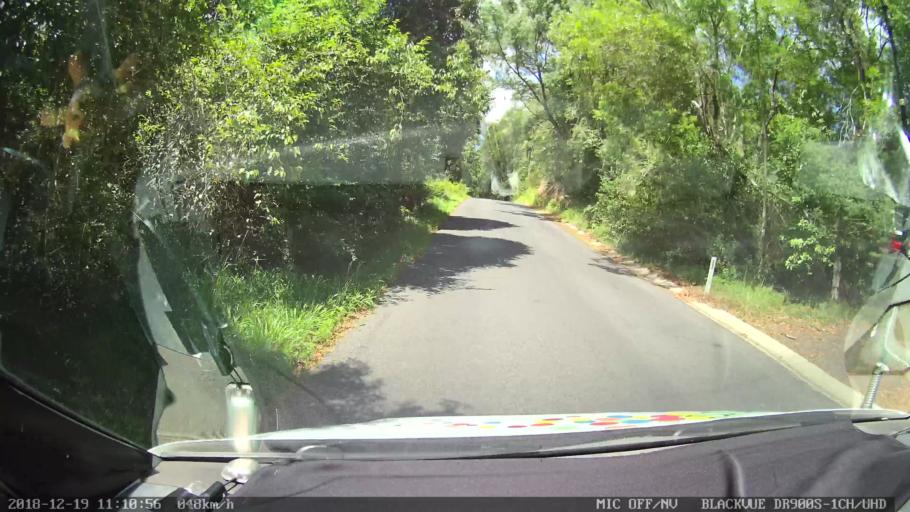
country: AU
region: New South Wales
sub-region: Lismore Municipality
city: Nimbin
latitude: -28.6409
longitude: 153.2594
